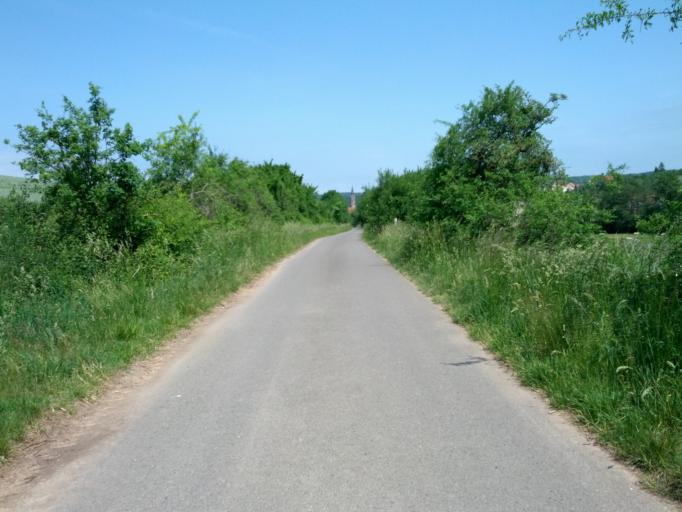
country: DE
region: Thuringia
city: Urnshausen
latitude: 50.7289
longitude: 10.1666
